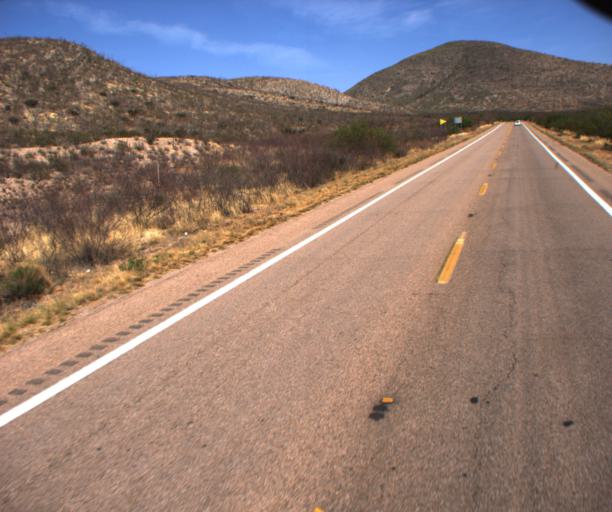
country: US
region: Arizona
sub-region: Cochise County
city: Bisbee
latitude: 31.5218
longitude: -110.0375
